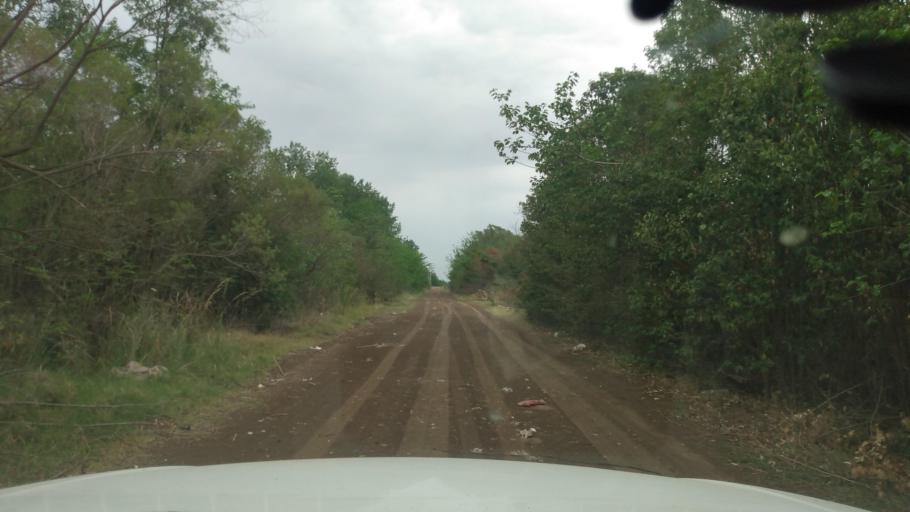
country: AR
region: Buenos Aires
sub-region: Partido de Lujan
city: Lujan
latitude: -34.5494
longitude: -59.1661
